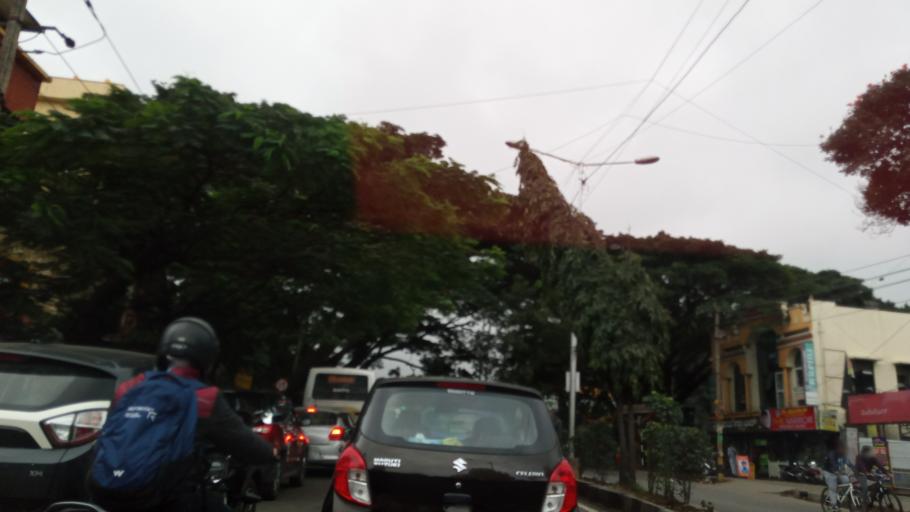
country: IN
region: Karnataka
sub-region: Bangalore Urban
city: Bangalore
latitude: 12.9287
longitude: 77.5456
